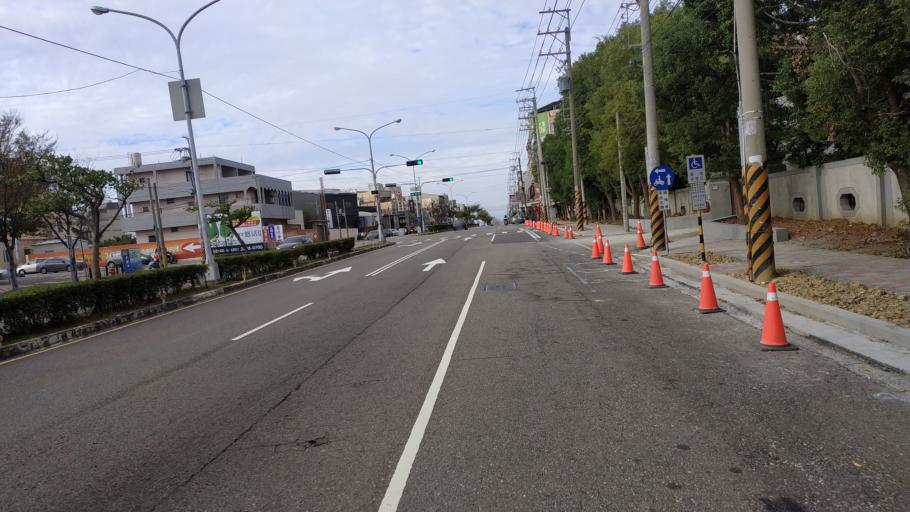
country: TW
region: Taiwan
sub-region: Taichung City
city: Taichung
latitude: 24.2260
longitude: 120.5682
